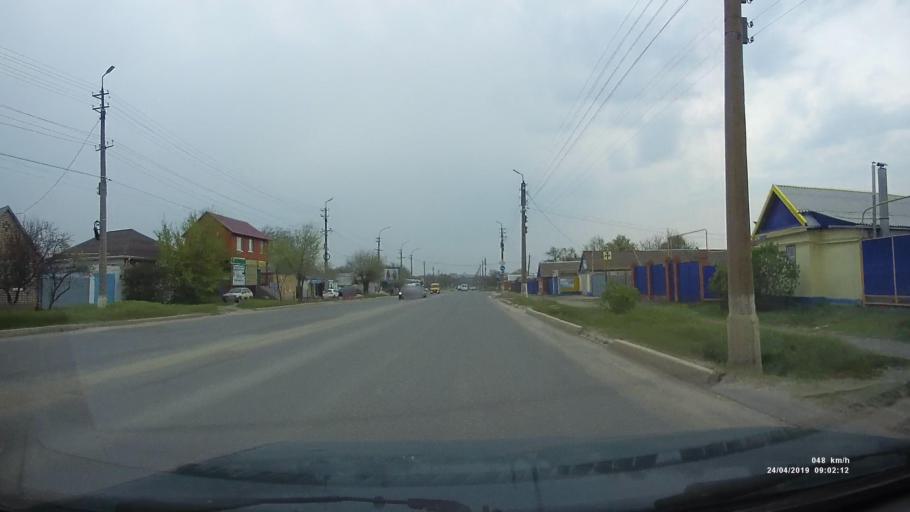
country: RU
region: Kalmykiya
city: Elista
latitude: 46.3121
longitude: 44.2319
